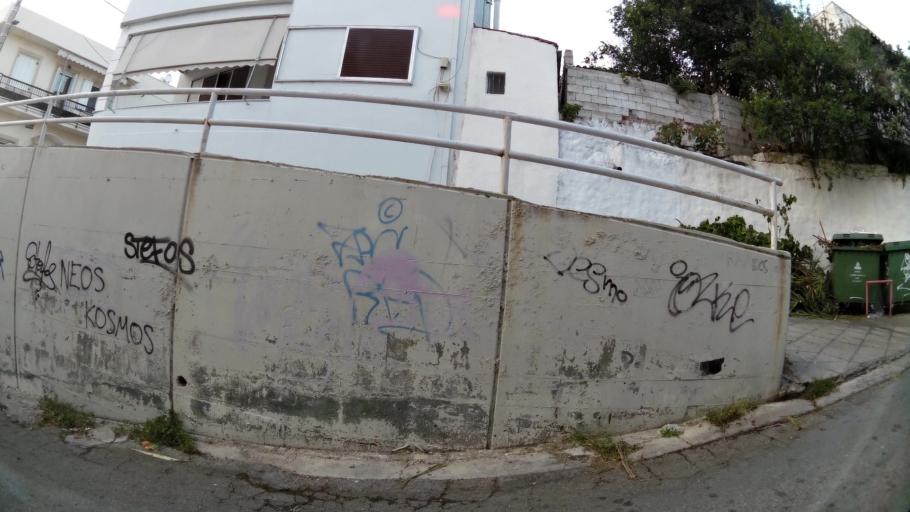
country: GR
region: Attica
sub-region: Nomarchia Athinas
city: Dhafni
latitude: 37.9545
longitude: 23.7310
